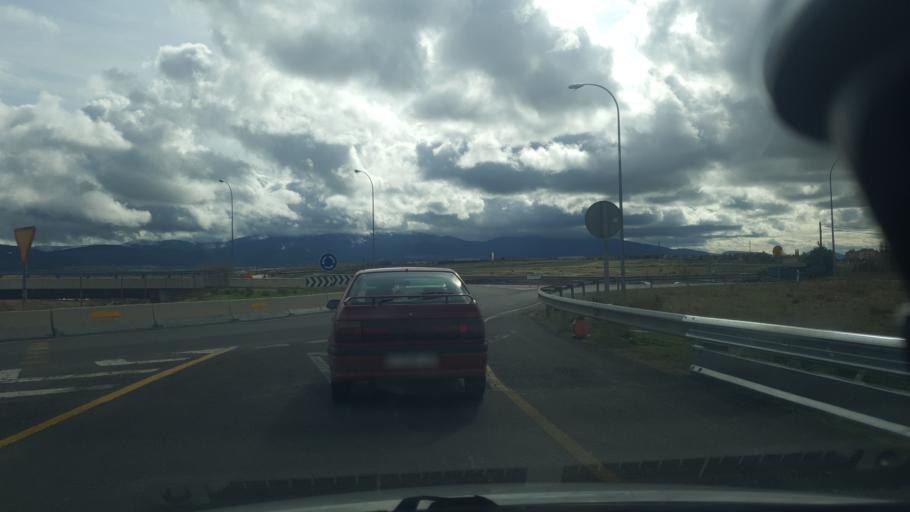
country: ES
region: Castille and Leon
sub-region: Provincia de Segovia
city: San Cristobal de Segovia
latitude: 40.9529
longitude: -4.0911
